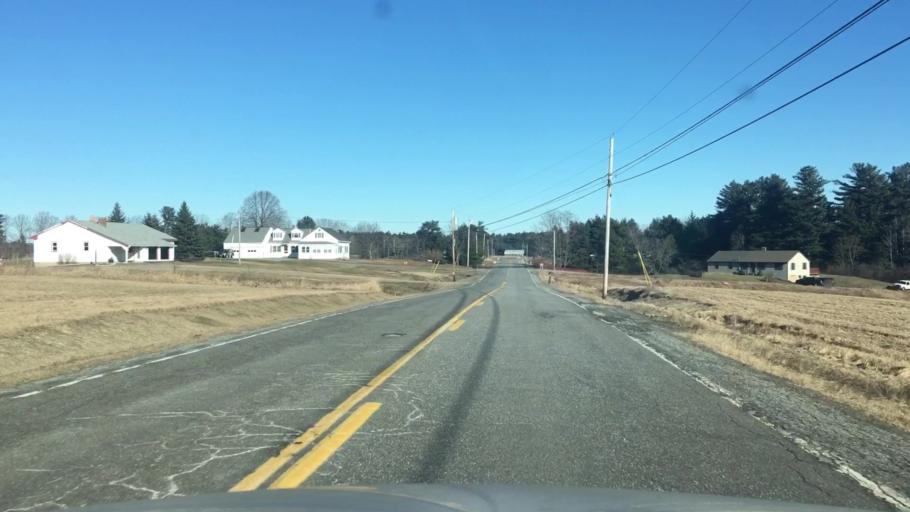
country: US
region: Maine
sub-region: Somerset County
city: Fairfield
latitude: 44.5610
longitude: -69.5794
